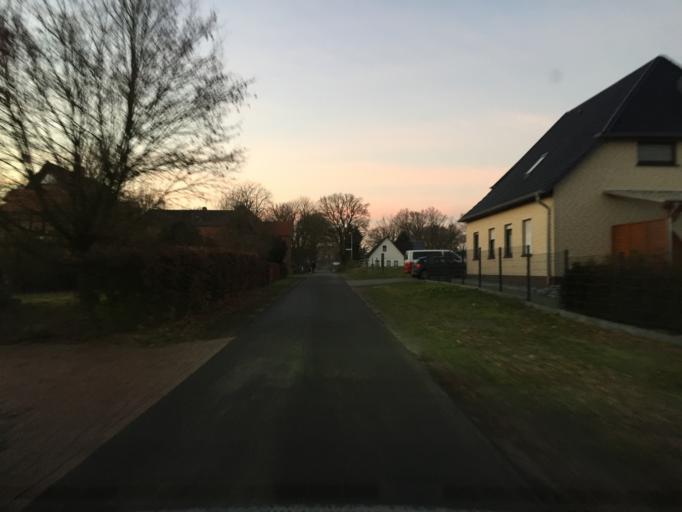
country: DE
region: Lower Saxony
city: Hassel
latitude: 52.6665
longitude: 8.8366
